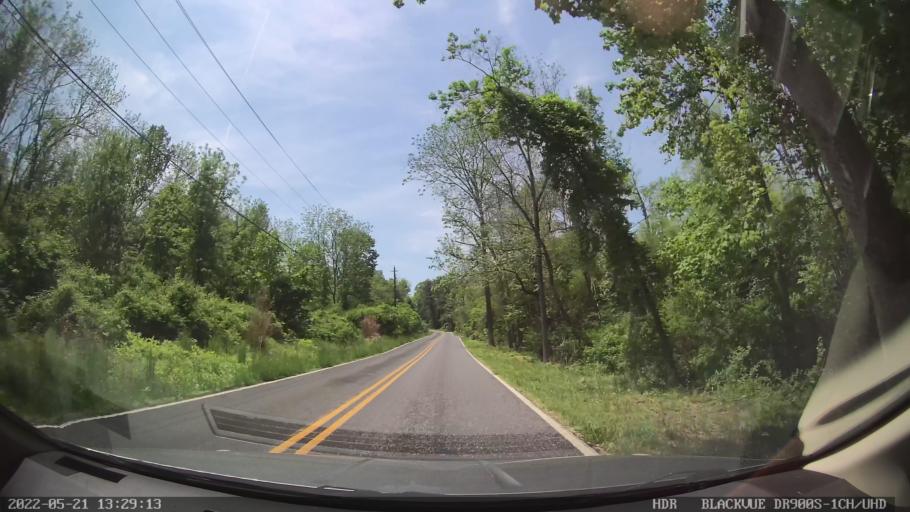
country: US
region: Pennsylvania
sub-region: Berks County
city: Bally
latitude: 40.4234
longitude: -75.6328
